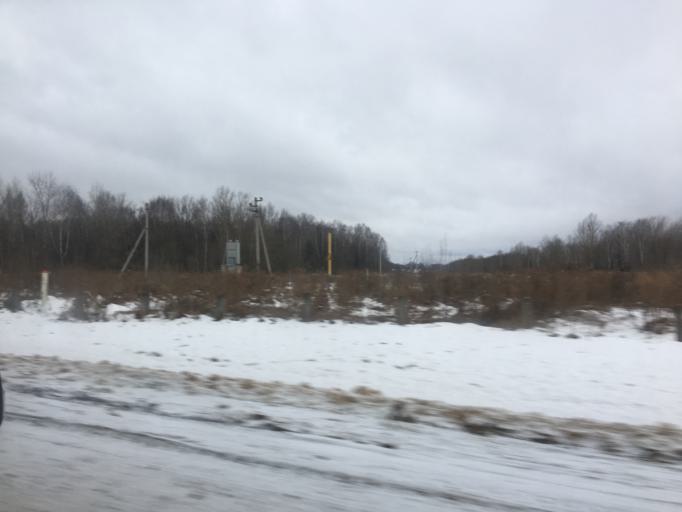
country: RU
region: Tula
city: Pervomayskiy
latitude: 54.0566
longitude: 37.5318
